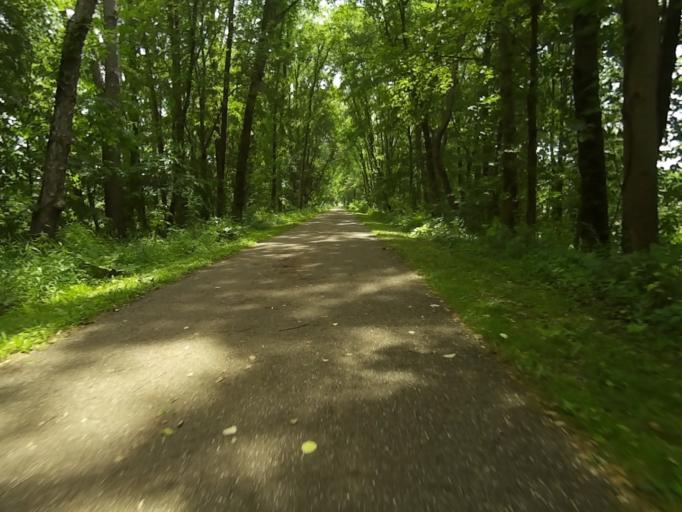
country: US
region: Ohio
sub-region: Portage County
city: Kent
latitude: 41.1882
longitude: -81.3860
